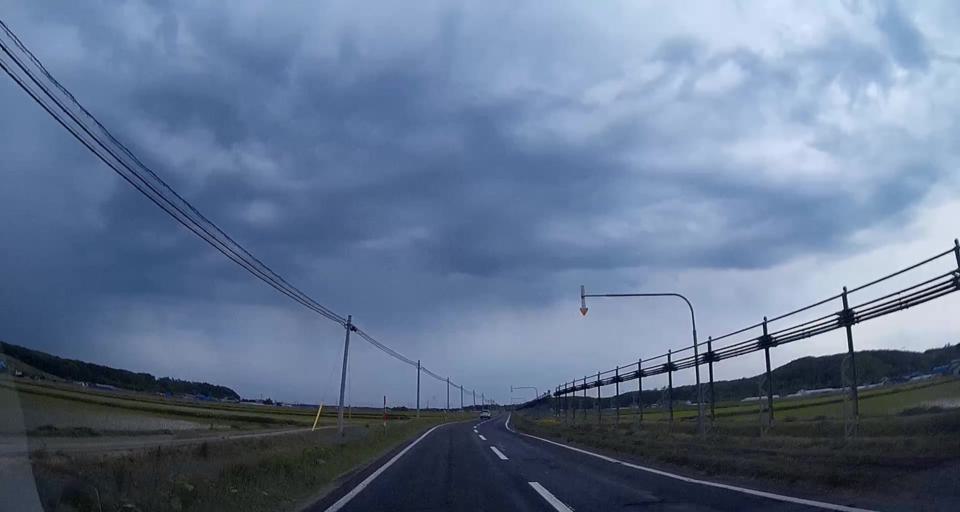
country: JP
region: Hokkaido
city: Chitose
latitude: 42.7188
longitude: 141.8694
